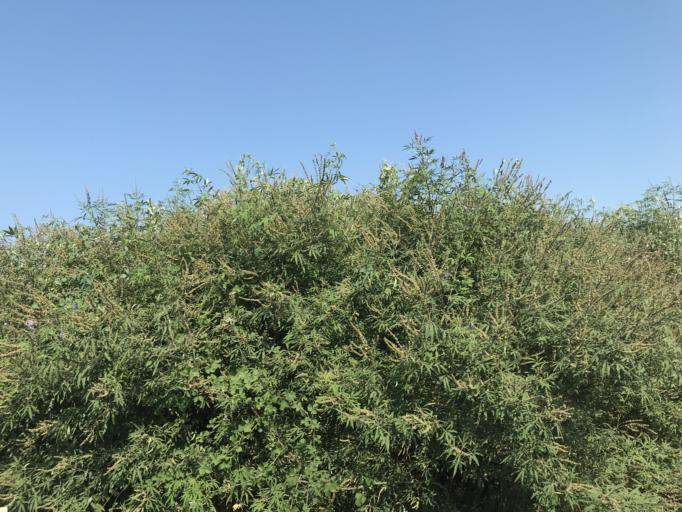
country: TR
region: Izmir
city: Selcuk
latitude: 37.9464
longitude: 27.3411
